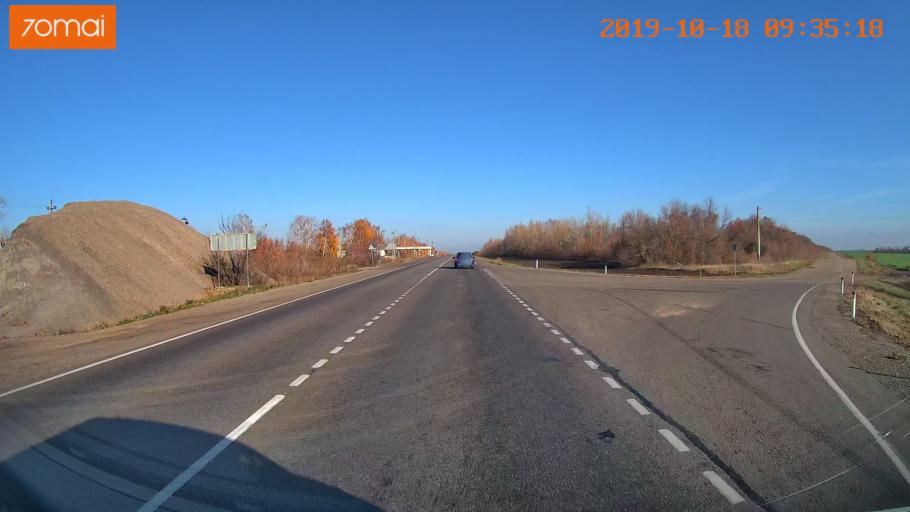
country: RU
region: Tula
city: Yefremov
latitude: 53.1907
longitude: 38.1490
